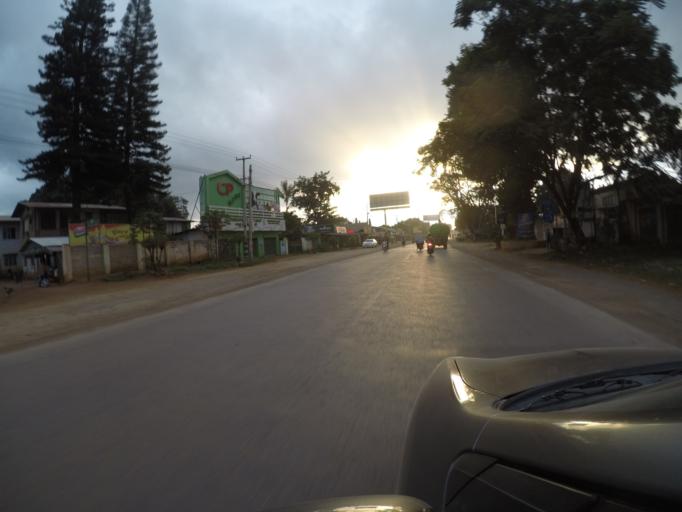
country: MM
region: Shan
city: Taunggyi
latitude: 20.7904
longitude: 97.0055
